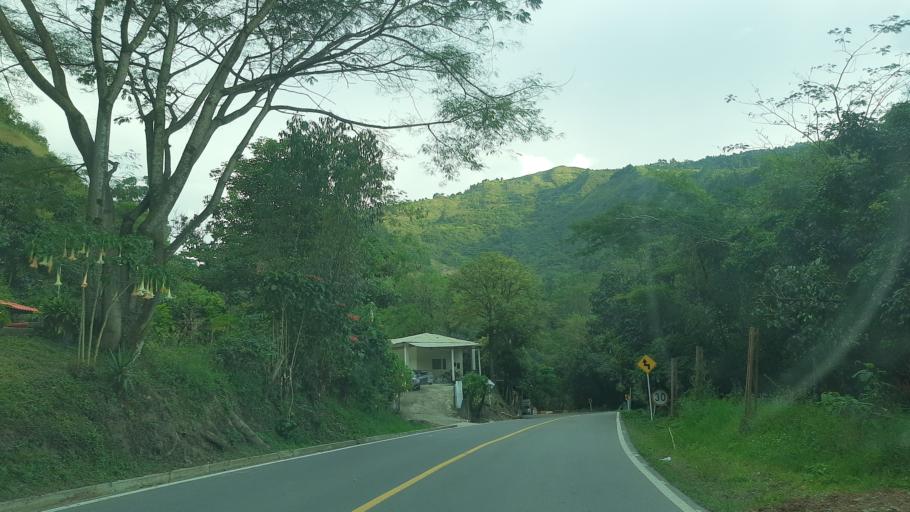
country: CO
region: Boyaca
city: Somondoco
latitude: 5.0093
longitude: -73.4237
